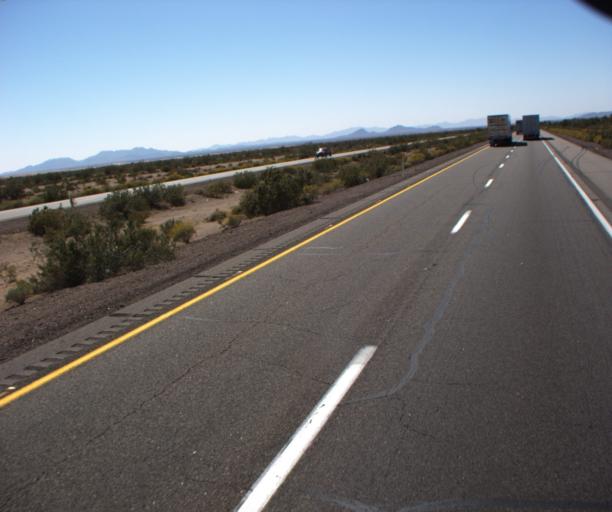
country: US
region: Arizona
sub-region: Yuma County
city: Wellton
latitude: 32.7222
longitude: -113.7652
